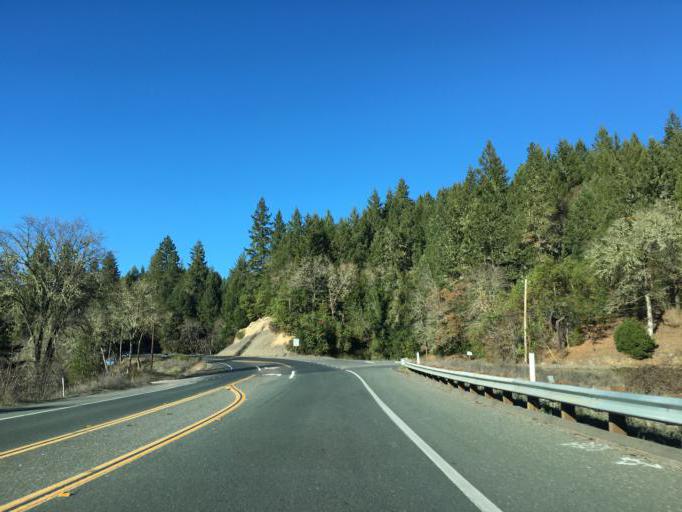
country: US
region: California
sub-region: Mendocino County
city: Brooktrails
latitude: 39.4636
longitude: -123.3505
